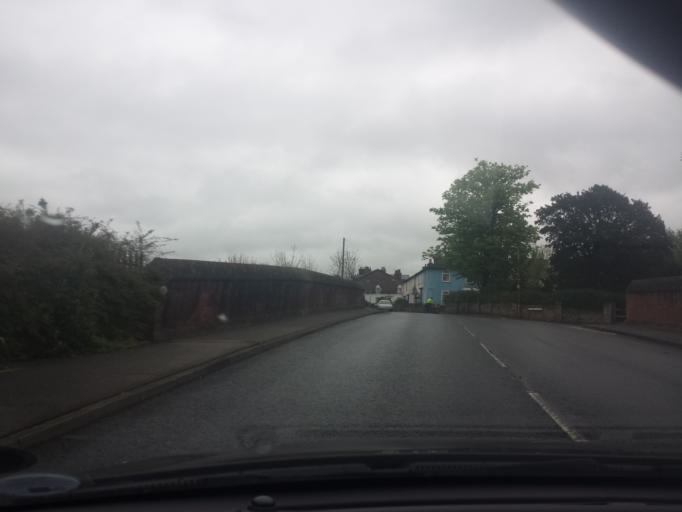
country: GB
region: England
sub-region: Essex
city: Mistley
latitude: 51.9439
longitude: 1.0828
